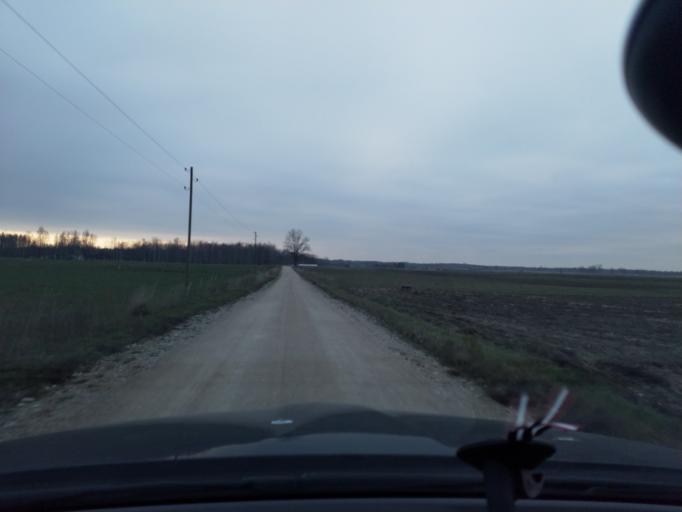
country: LV
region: Rucavas
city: Rucava
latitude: 56.2464
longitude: 21.2624
